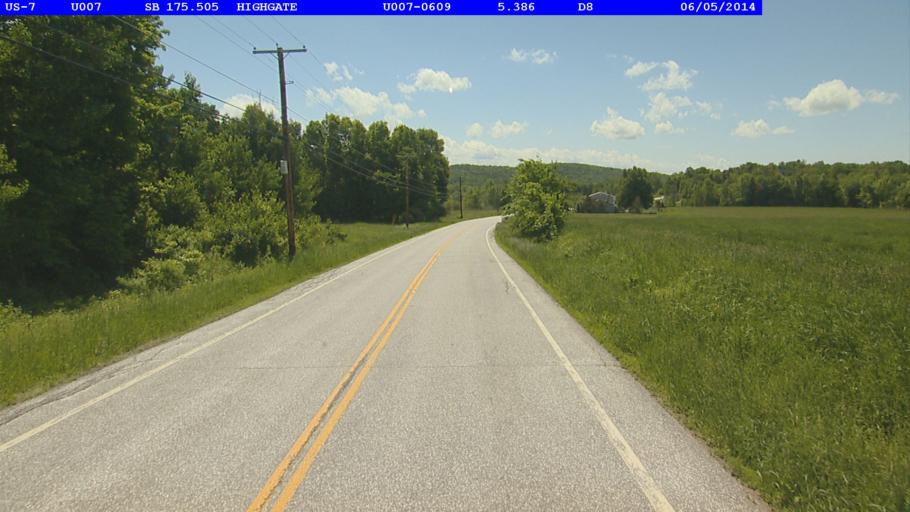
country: US
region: Vermont
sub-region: Franklin County
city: Swanton
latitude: 45.0026
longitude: -73.0790
